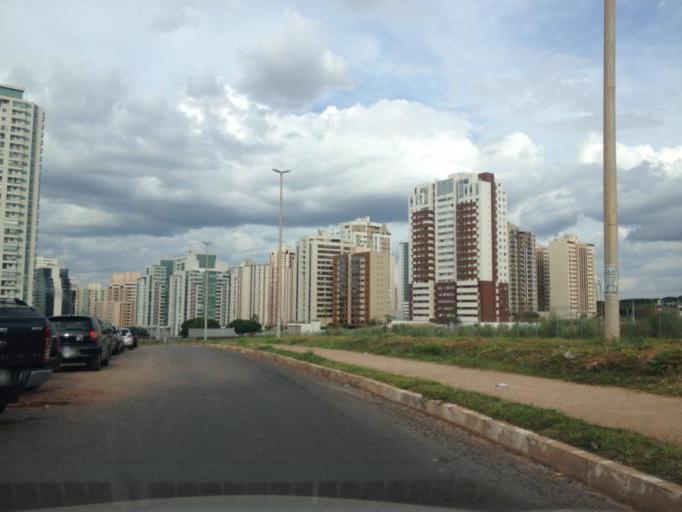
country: BR
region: Federal District
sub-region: Brasilia
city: Brasilia
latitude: -15.8392
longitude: -48.0327
